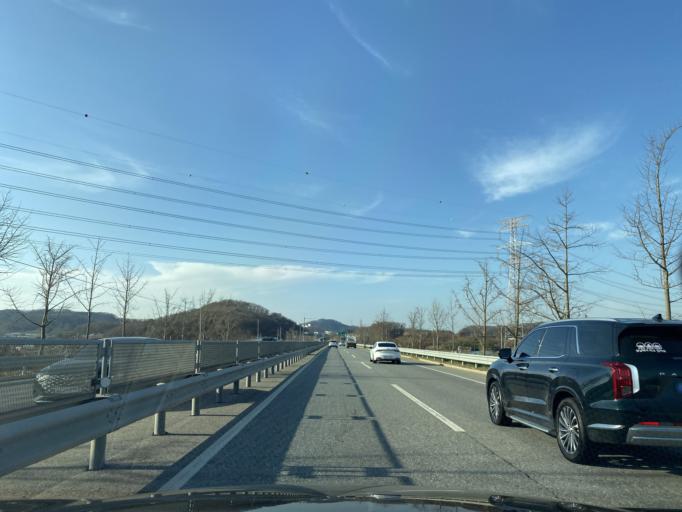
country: KR
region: Chungcheongnam-do
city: Asan
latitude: 36.7605
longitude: 126.9550
